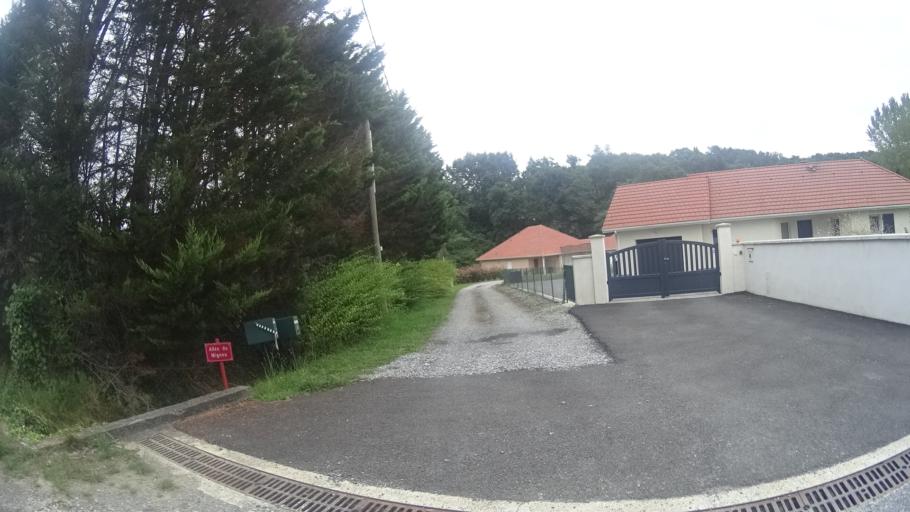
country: FR
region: Aquitaine
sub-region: Departement des Pyrenees-Atlantiques
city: Mont
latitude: 43.4875
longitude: -0.6955
